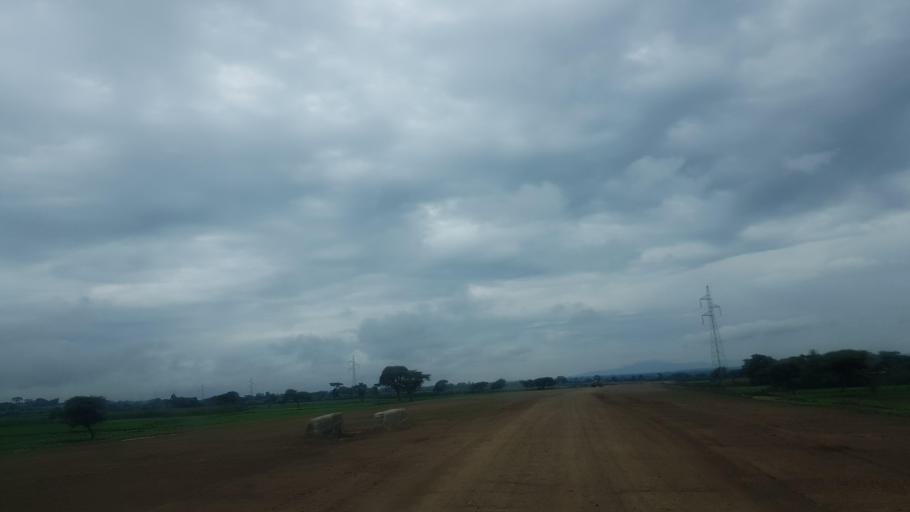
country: ET
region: Oromiya
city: Shashemene
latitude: 7.3925
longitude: 38.6562
